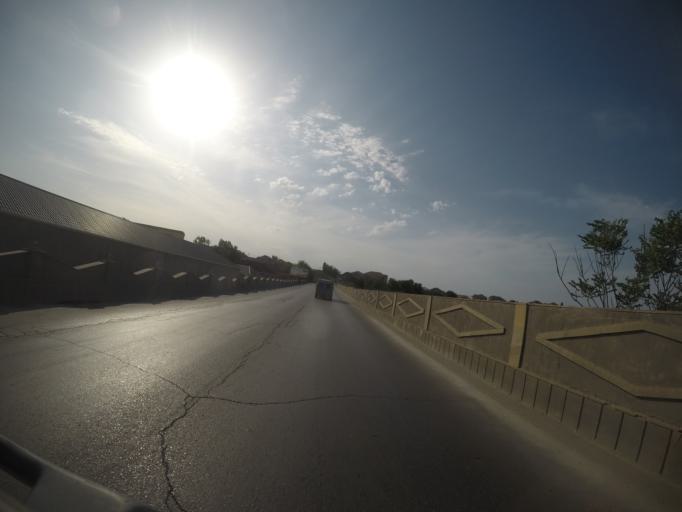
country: AZ
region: Baki
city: Binagadi
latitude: 40.4695
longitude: 49.8392
